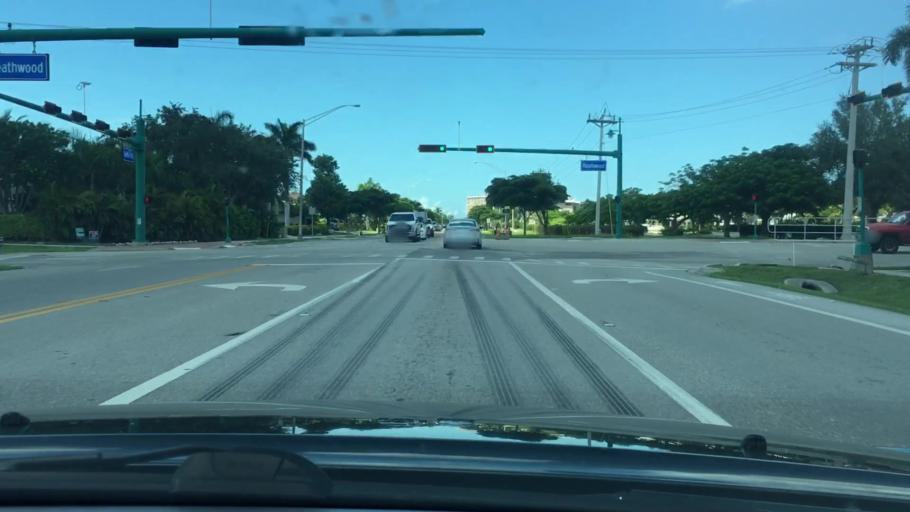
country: US
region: Florida
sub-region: Collier County
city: Marco
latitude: 25.9371
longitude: -81.7155
